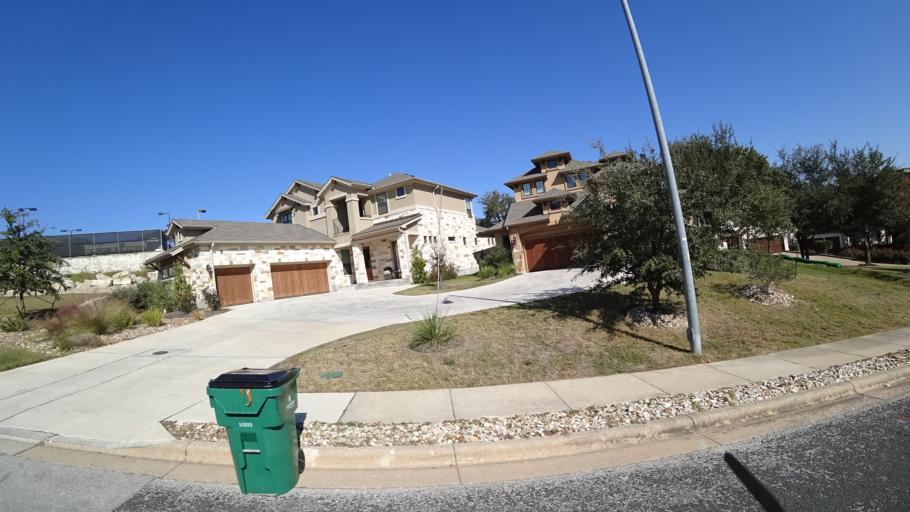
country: US
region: Texas
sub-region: Travis County
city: Lost Creek
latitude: 30.3666
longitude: -97.8608
